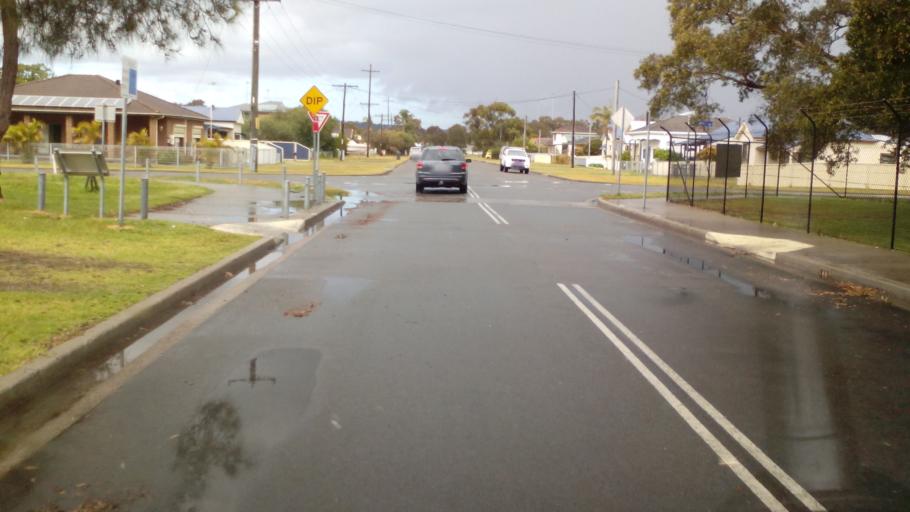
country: AU
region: New South Wales
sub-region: Lake Macquarie Shire
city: Belmont South
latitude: -33.0755
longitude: 151.6363
